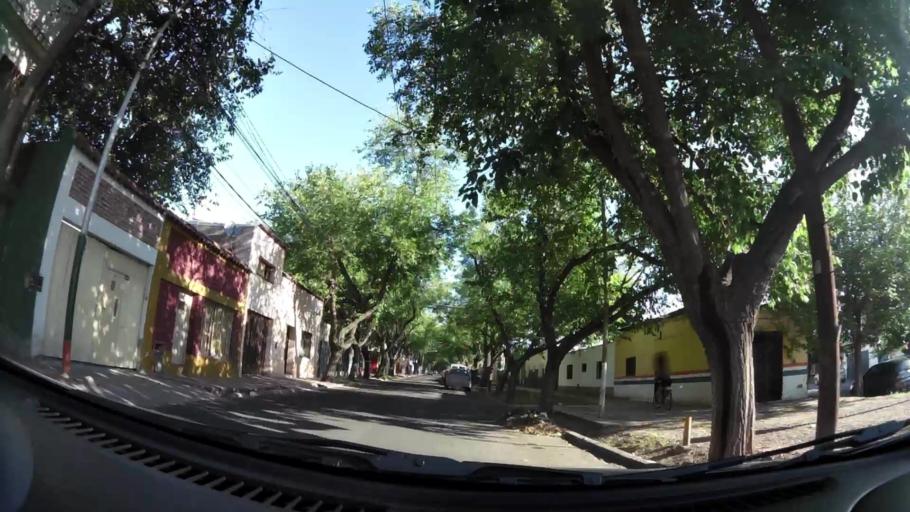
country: AR
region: Mendoza
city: Mendoza
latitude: -32.9075
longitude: -68.8288
